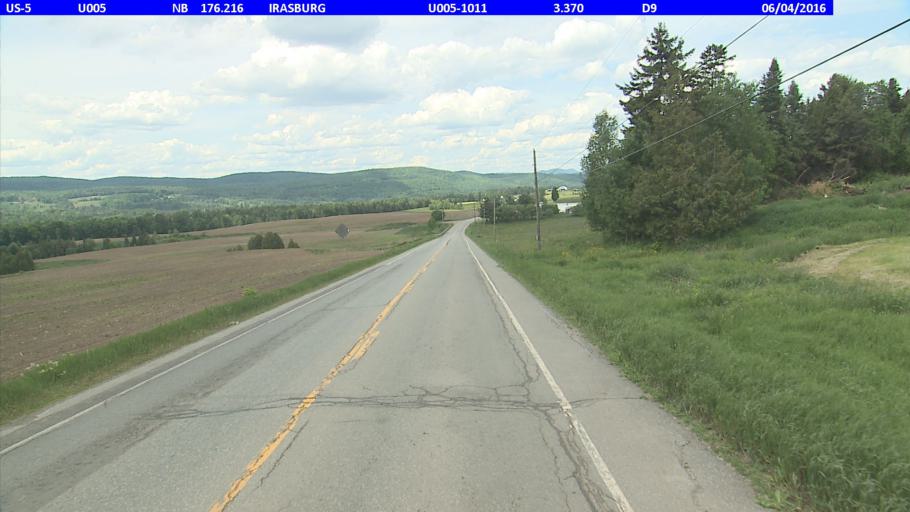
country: US
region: Vermont
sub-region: Orleans County
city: Newport
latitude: 44.8405
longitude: -72.2602
